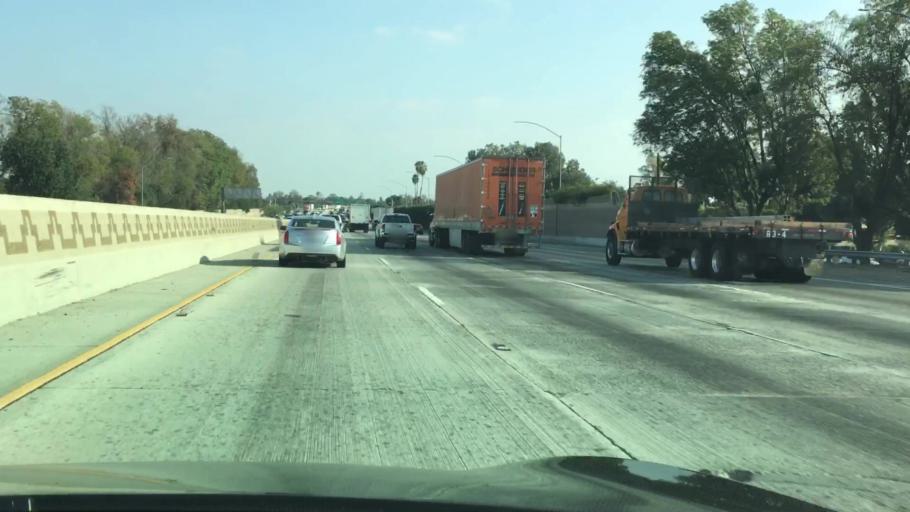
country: US
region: California
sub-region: Los Angeles County
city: Santa Fe Springs
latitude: 33.9570
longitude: -118.1106
